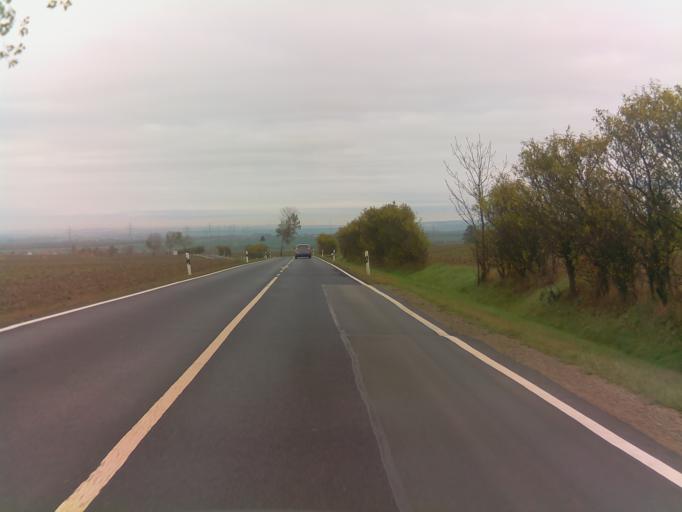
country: DE
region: Thuringia
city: Behringen
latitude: 50.8023
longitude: 11.0336
